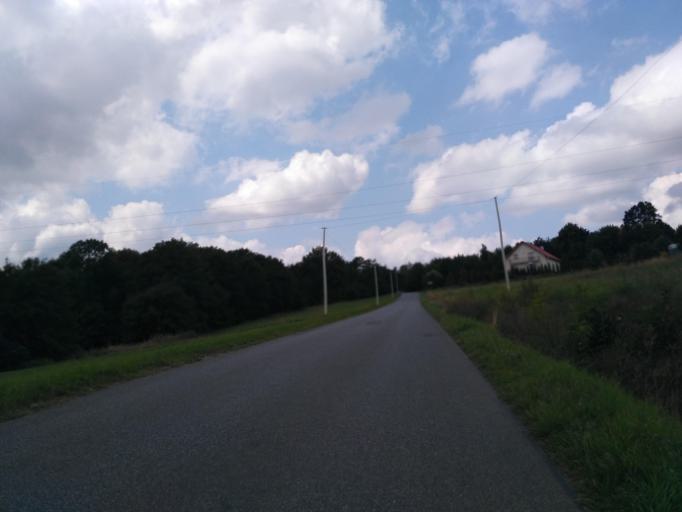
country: PL
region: Subcarpathian Voivodeship
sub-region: Powiat krosnienski
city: Iwonicz-Zdroj
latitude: 49.5837
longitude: 21.7471
